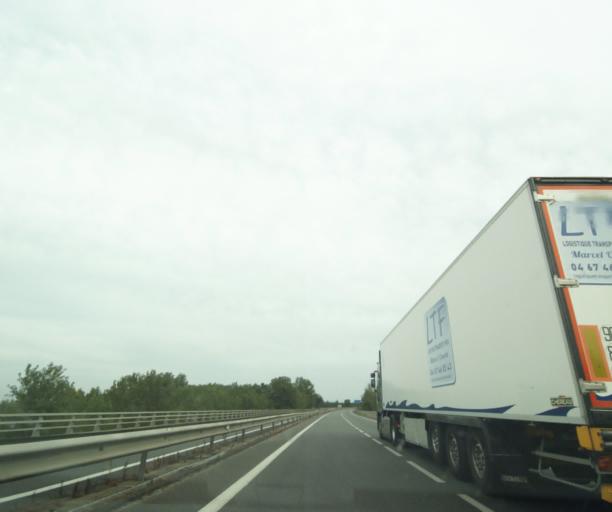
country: FR
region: Aquitaine
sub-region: Departement du Lot-et-Garonne
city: Boe
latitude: 44.1612
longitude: 0.6089
